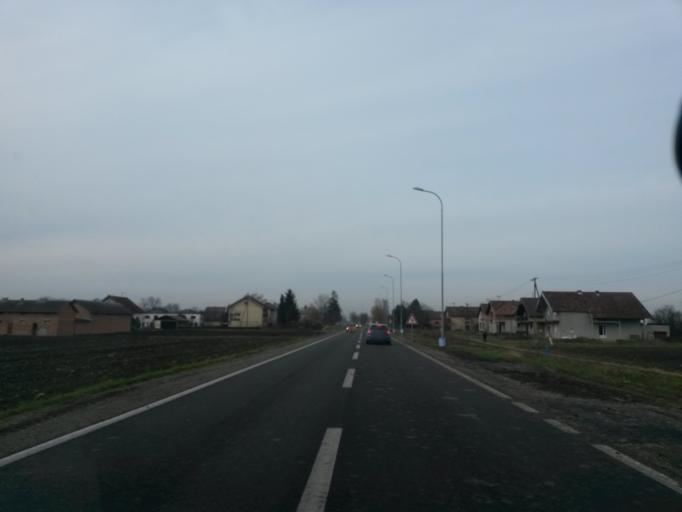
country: HR
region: Osjecko-Baranjska
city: Sarvas
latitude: 45.4729
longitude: 18.8365
